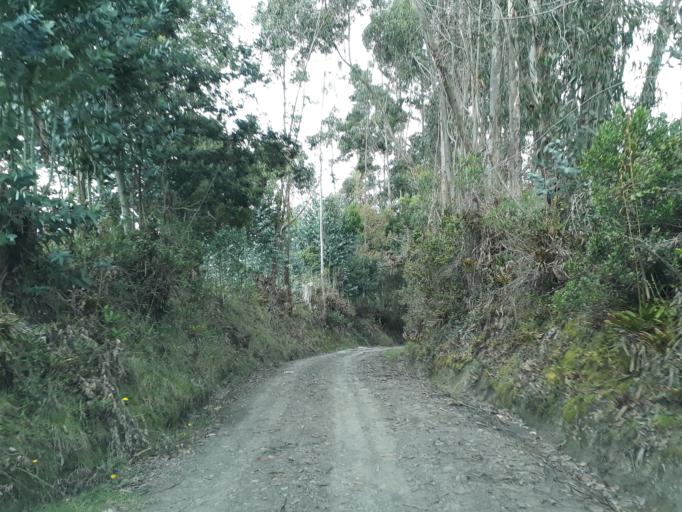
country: CO
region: Cundinamarca
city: Simijaca
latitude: 5.4786
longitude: -73.8851
